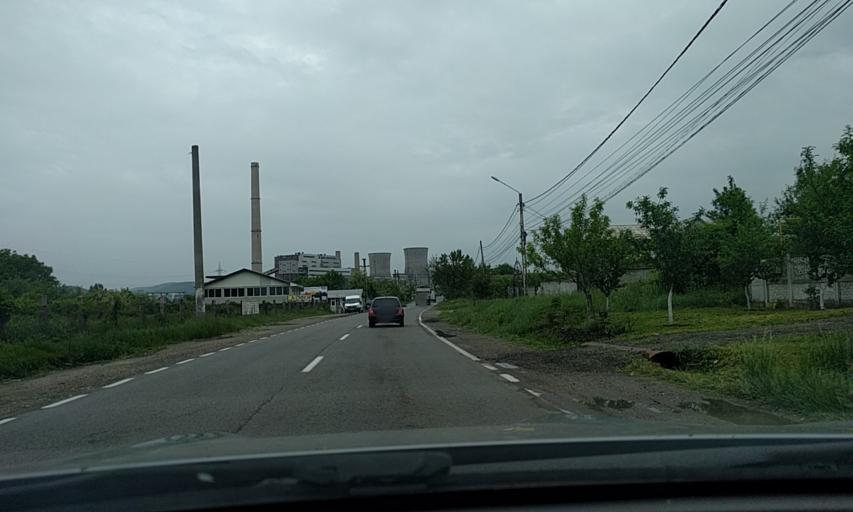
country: RO
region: Dambovita
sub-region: Comuna Doicesti
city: Doicesti
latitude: 44.9946
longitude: 25.4047
